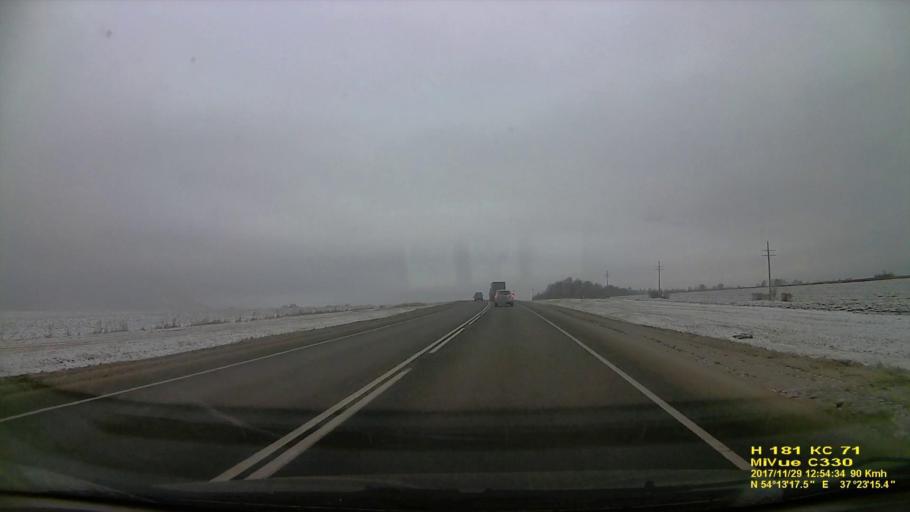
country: RU
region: Tula
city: Leninskiy
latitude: 54.2214
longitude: 37.3878
